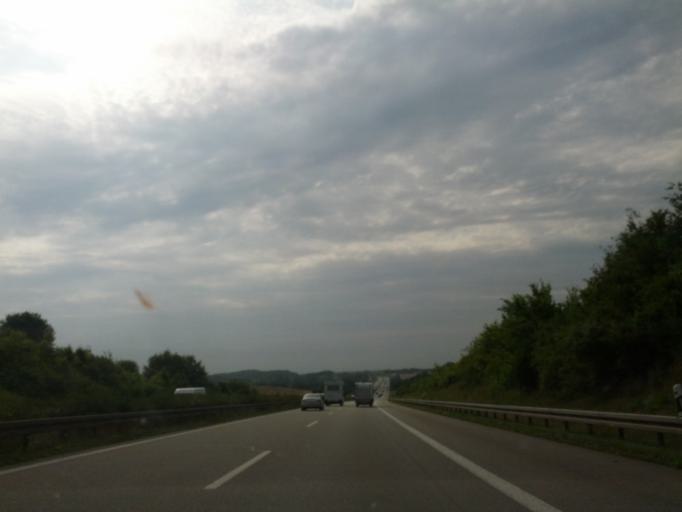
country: DE
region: Mecklenburg-Vorpommern
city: Papendorf
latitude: 54.0192
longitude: 12.1491
